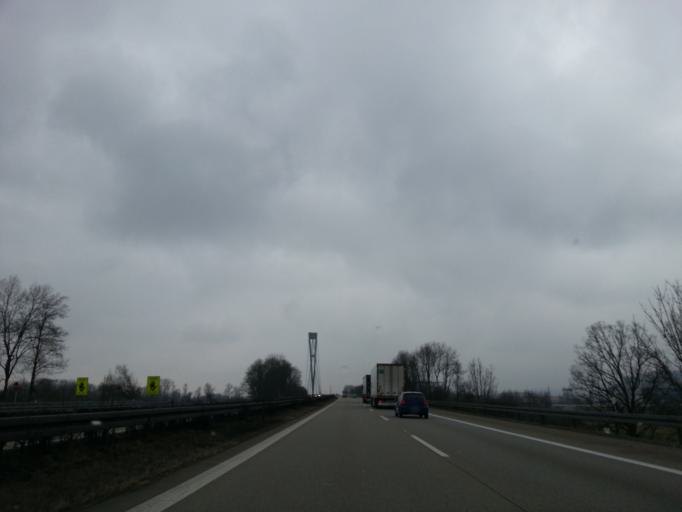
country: DE
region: Bavaria
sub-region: Lower Bavaria
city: Deggendorf
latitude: 48.8038
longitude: 12.9804
